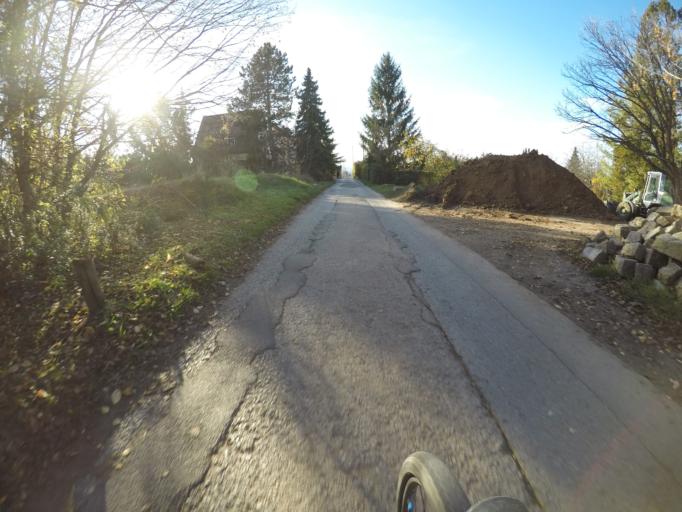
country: DE
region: Baden-Wuerttemberg
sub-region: Regierungsbezirk Stuttgart
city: Fellbach
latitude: 48.8151
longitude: 9.2540
